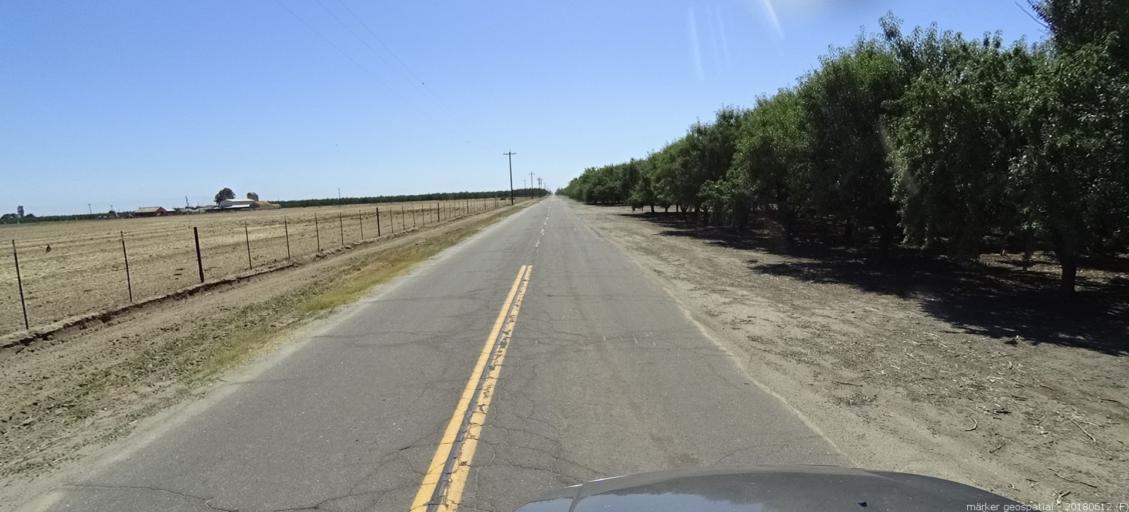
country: US
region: California
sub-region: Madera County
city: Chowchilla
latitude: 37.0326
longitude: -120.3277
